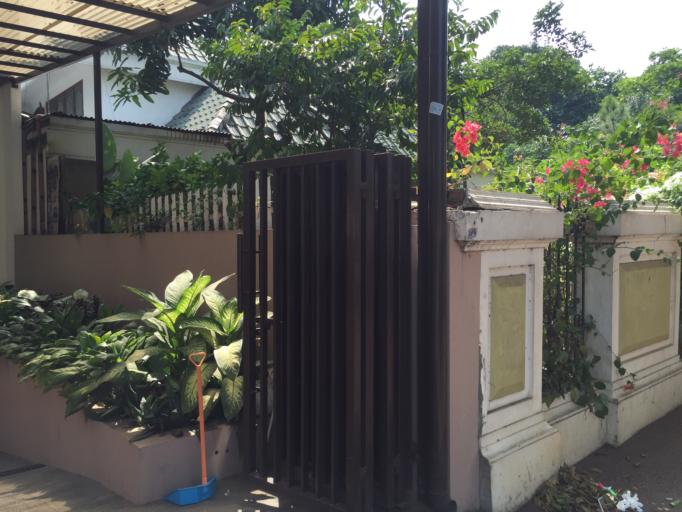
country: ID
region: Jakarta Raya
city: Jakarta
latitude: -6.2040
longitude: 106.8313
